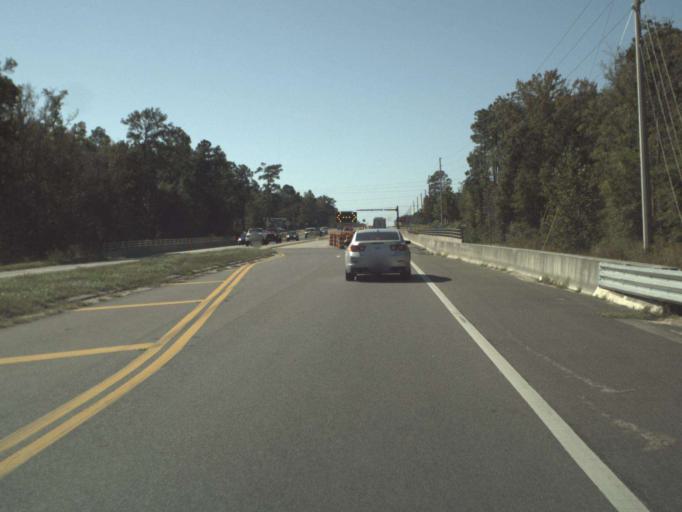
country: US
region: Florida
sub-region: Walton County
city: Freeport
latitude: 30.4937
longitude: -86.1204
